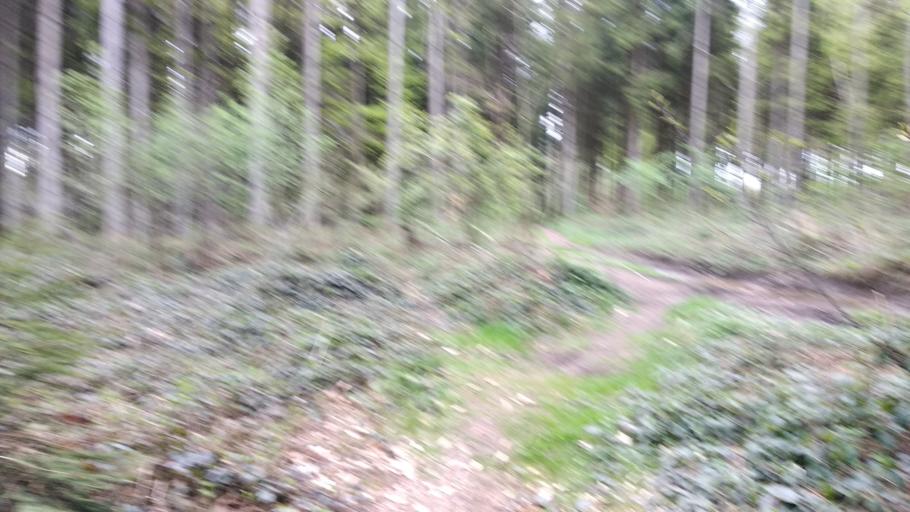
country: DE
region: Bavaria
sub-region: Swabia
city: Woringen
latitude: 47.9251
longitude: 10.1896
